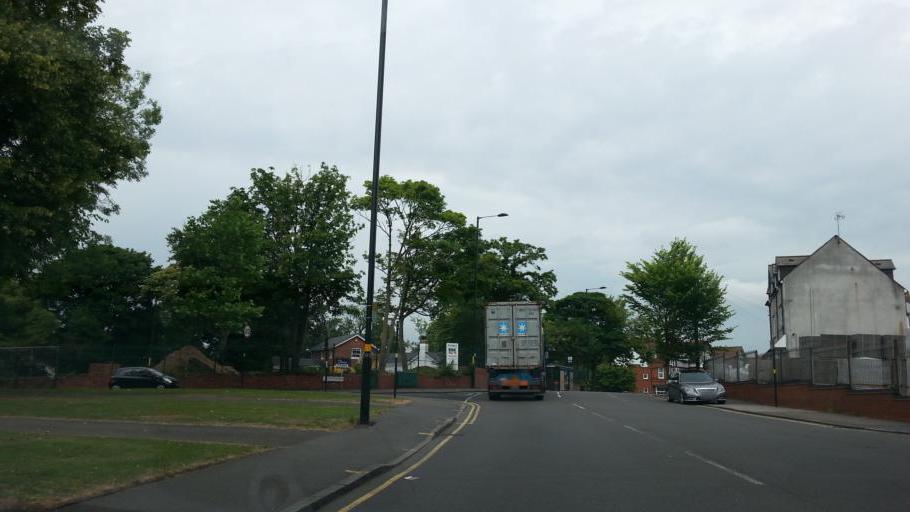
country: GB
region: England
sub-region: City and Borough of Birmingham
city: Birmingham
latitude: 52.4418
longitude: -1.8921
